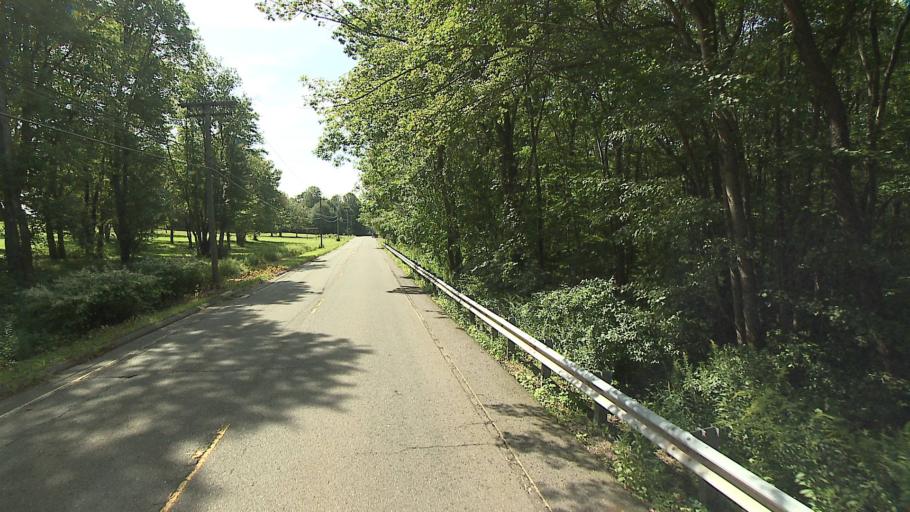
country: US
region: Connecticut
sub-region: Litchfield County
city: Plymouth
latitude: 41.6348
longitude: -73.0506
